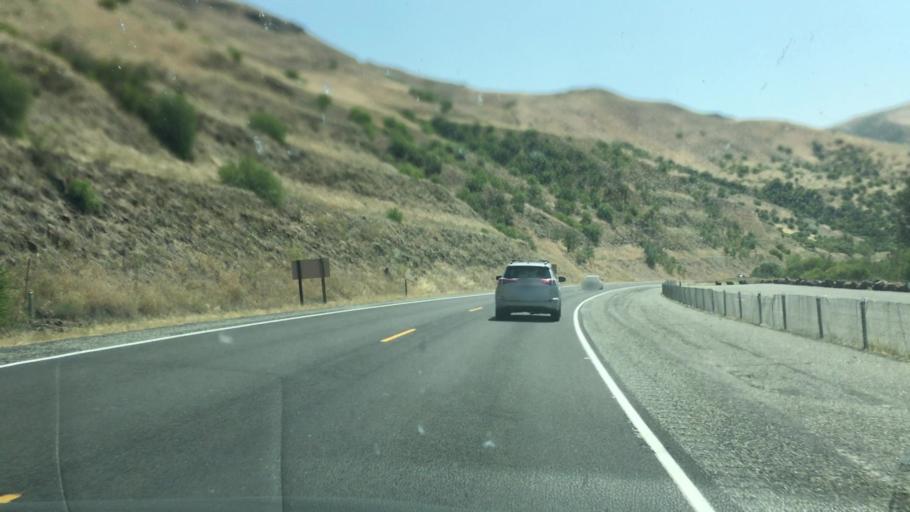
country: US
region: Idaho
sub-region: Idaho County
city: Grangeville
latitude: 45.7342
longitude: -116.3043
